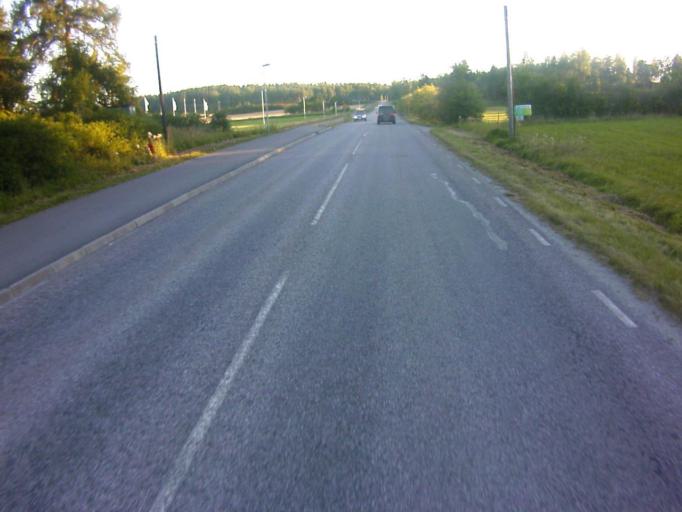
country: SE
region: Soedermanland
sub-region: Eskilstuna Kommun
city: Torshalla
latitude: 59.4125
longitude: 16.4399
